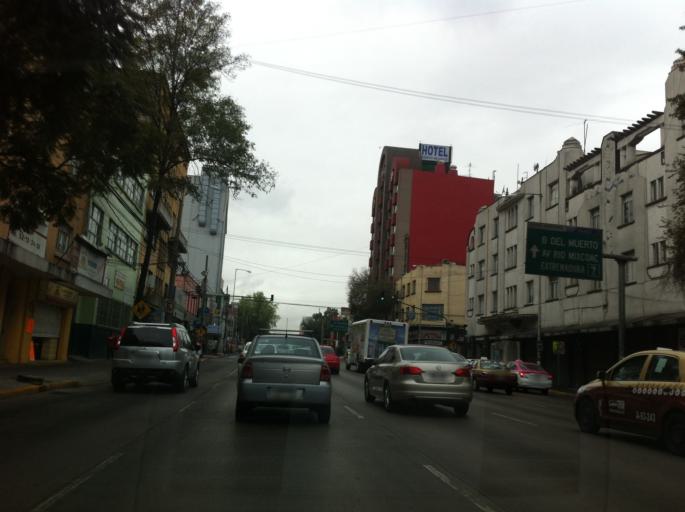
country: MX
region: Mexico City
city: Polanco
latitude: 19.4040
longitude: -99.1845
